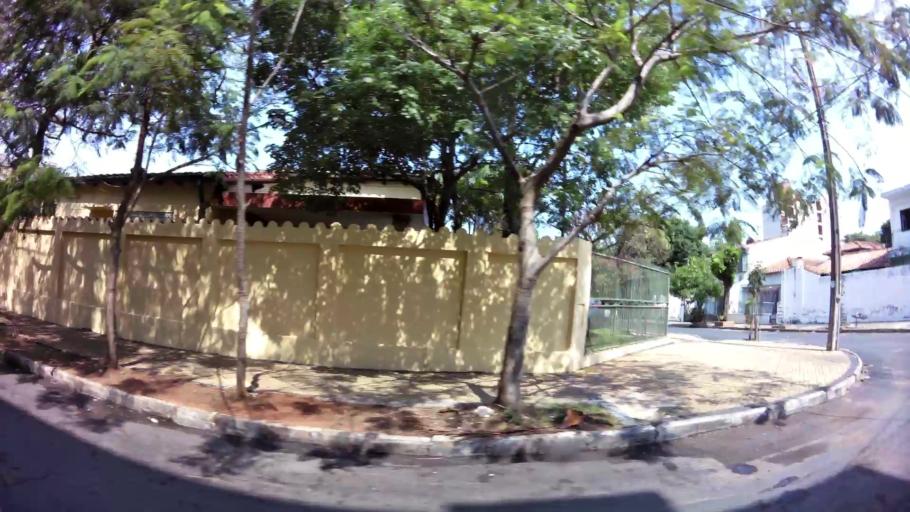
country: PY
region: Asuncion
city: Asuncion
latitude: -25.2896
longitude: -57.6528
